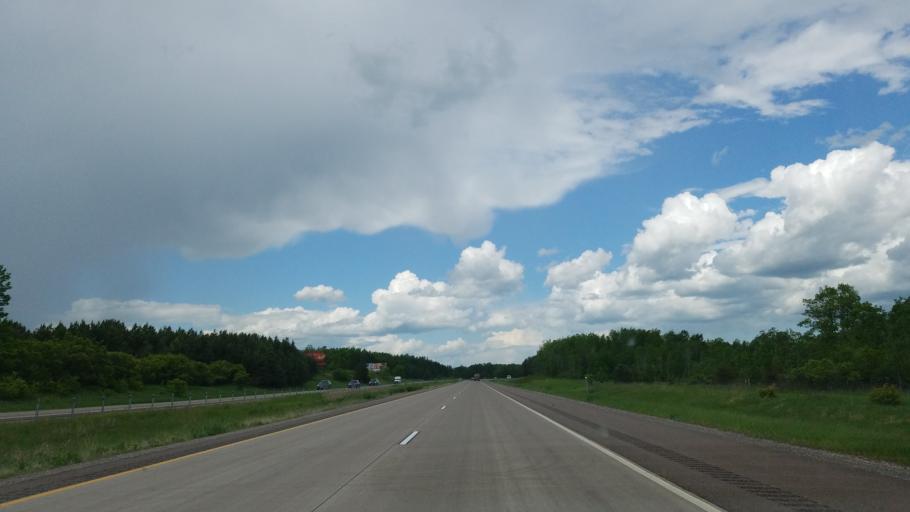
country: US
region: Minnesota
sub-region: Carlton County
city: Moose Lake
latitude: 46.4802
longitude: -92.7108
